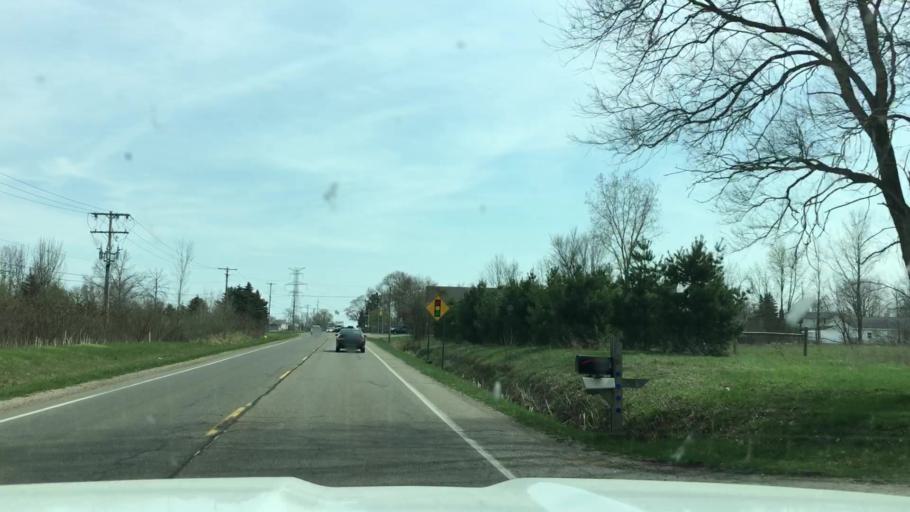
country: US
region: Michigan
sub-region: Ottawa County
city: Hudsonville
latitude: 42.8875
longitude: -85.9016
